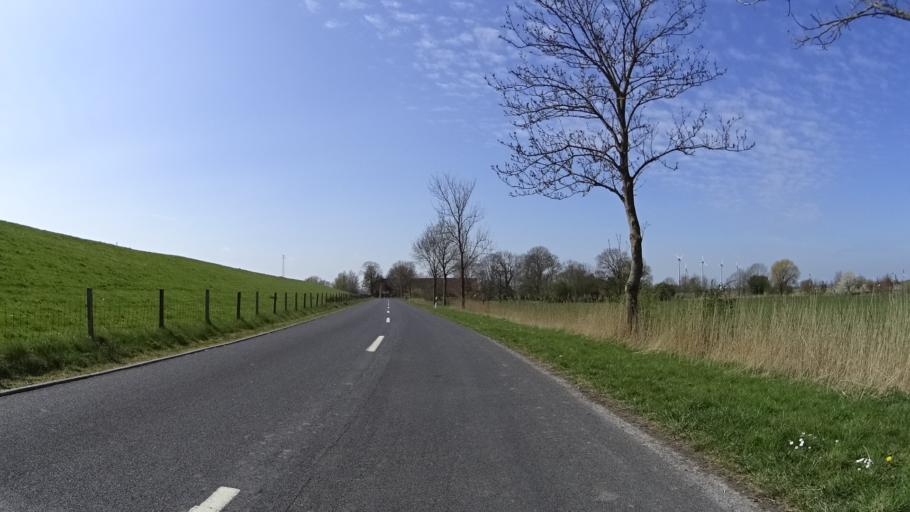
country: DE
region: Lower Saxony
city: Weener
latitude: 53.1868
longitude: 7.3950
